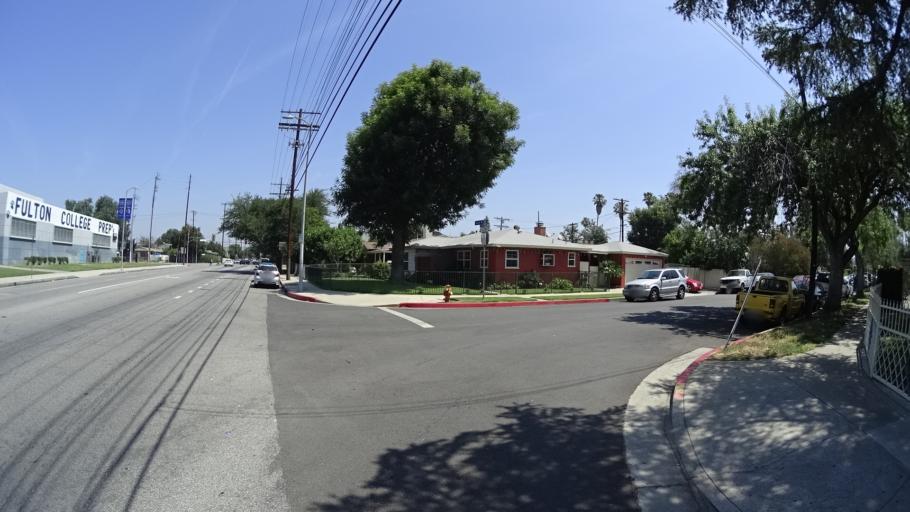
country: US
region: California
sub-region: Los Angeles County
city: Van Nuys
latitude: 34.2074
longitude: -118.4574
